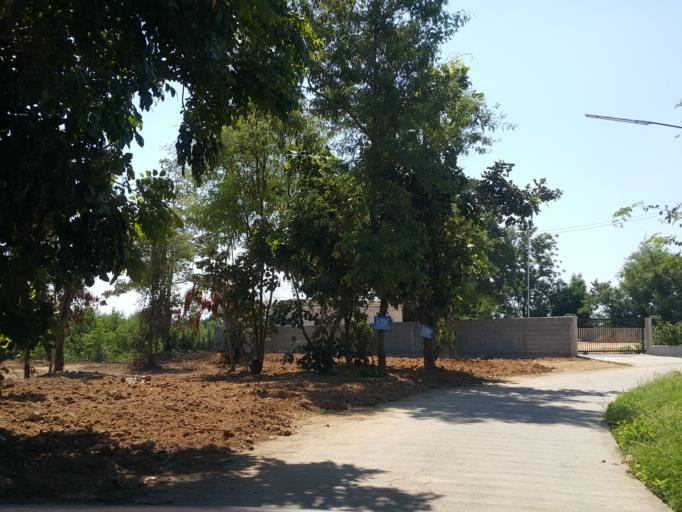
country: TH
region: Chiang Mai
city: Saraphi
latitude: 18.7622
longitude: 99.0599
